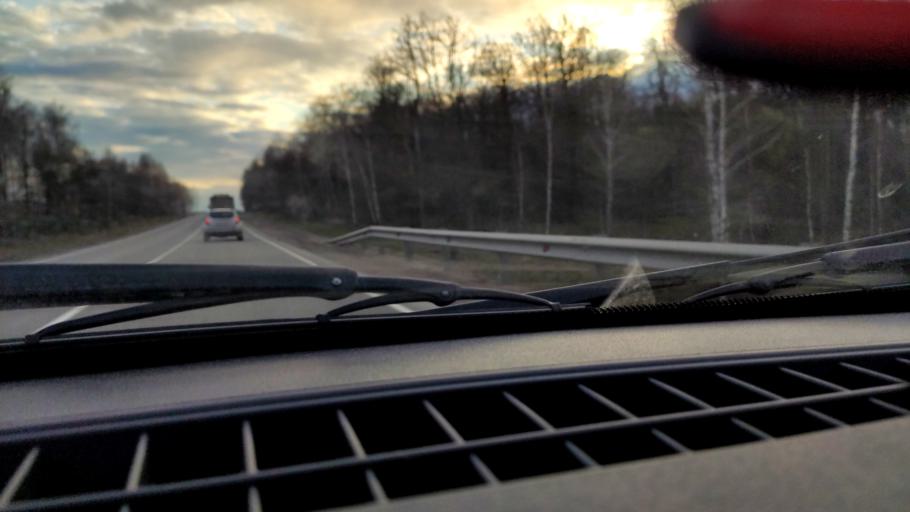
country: RU
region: Bashkortostan
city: Iglino
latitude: 54.7839
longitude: 56.5249
